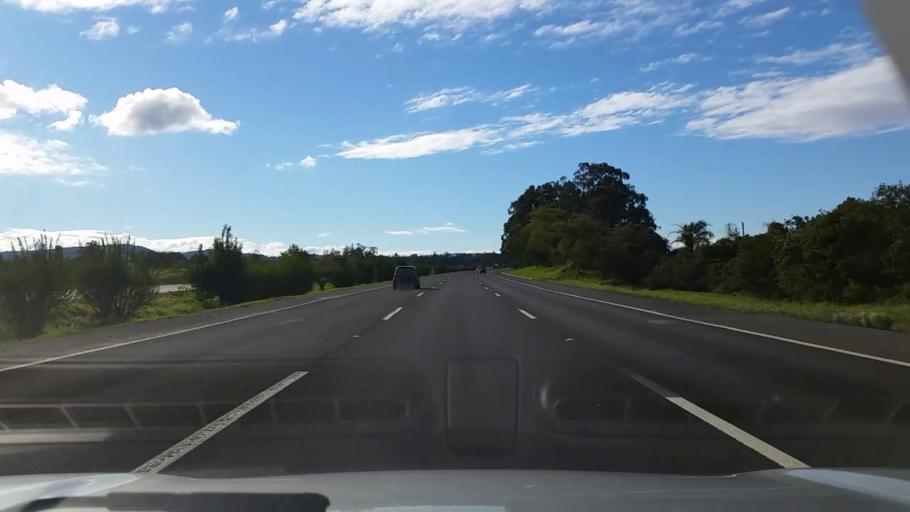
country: BR
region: Rio Grande do Sul
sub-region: Rolante
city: Rolante
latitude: -29.8795
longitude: -50.5086
